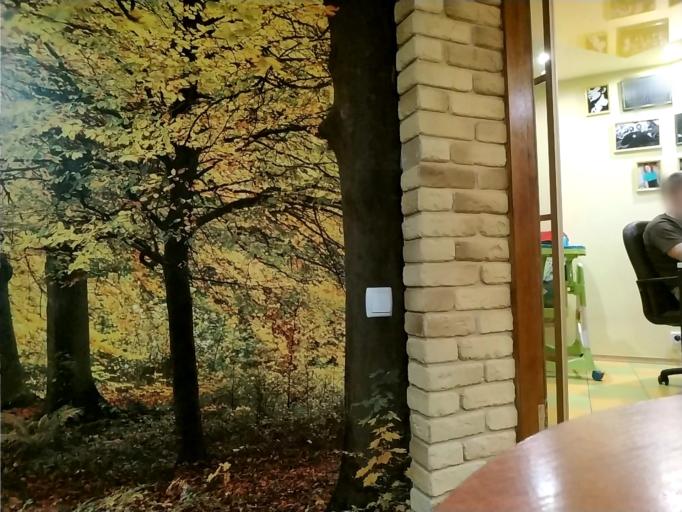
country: RU
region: Tverskaya
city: Zapadnaya Dvina
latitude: 56.3203
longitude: 31.9273
